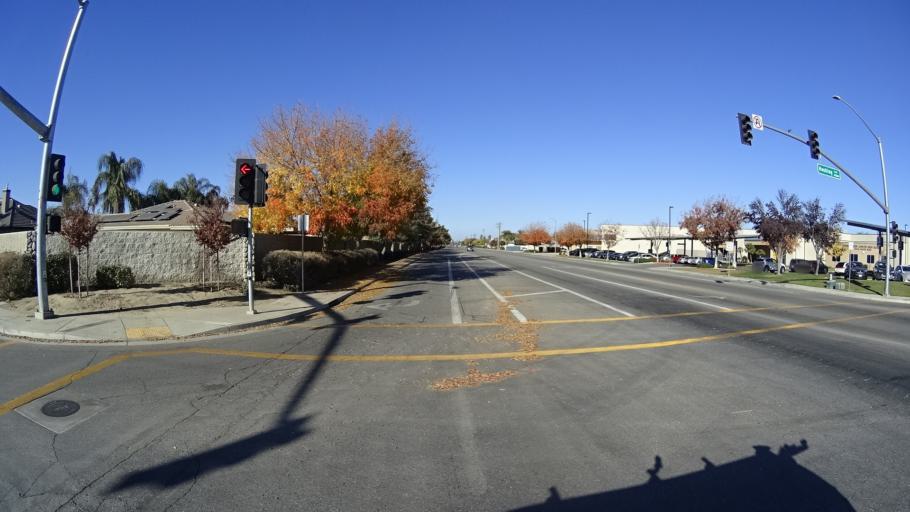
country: US
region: California
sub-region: Kern County
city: Greenfield
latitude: 35.2816
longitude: -119.0479
